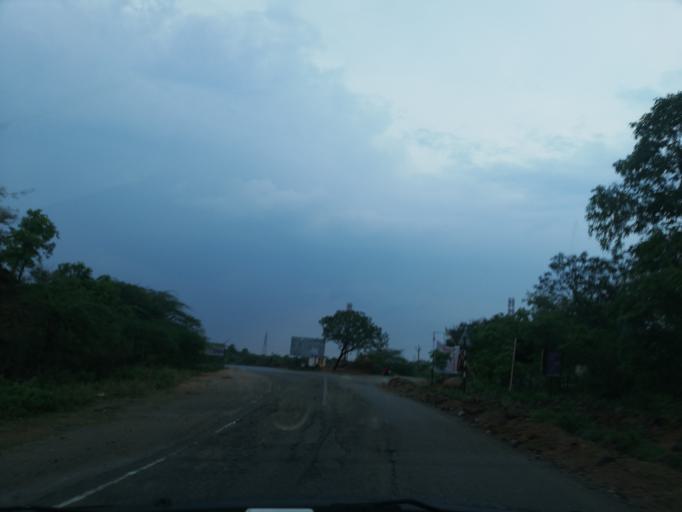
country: IN
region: Andhra Pradesh
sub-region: Guntur
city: Macherla
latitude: 16.6626
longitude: 79.2865
